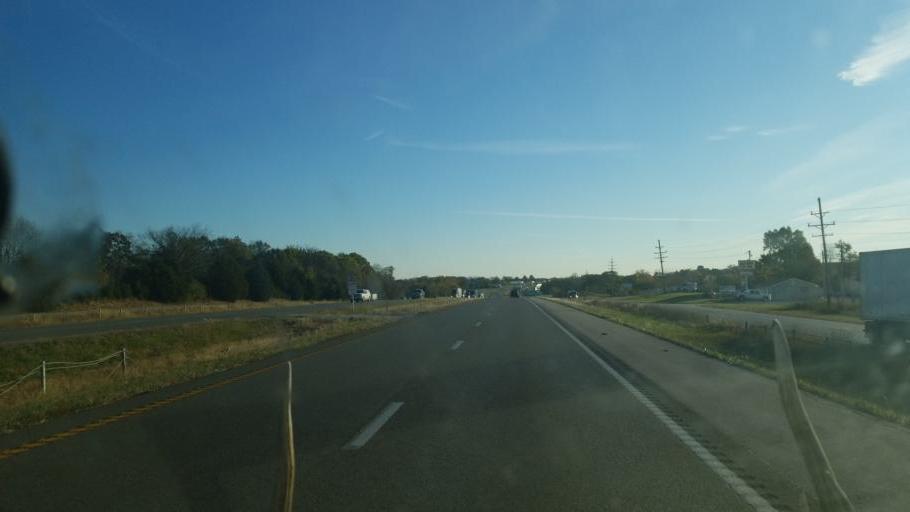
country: US
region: Missouri
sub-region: Warren County
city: Wright City
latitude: 38.8251
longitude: -91.0665
